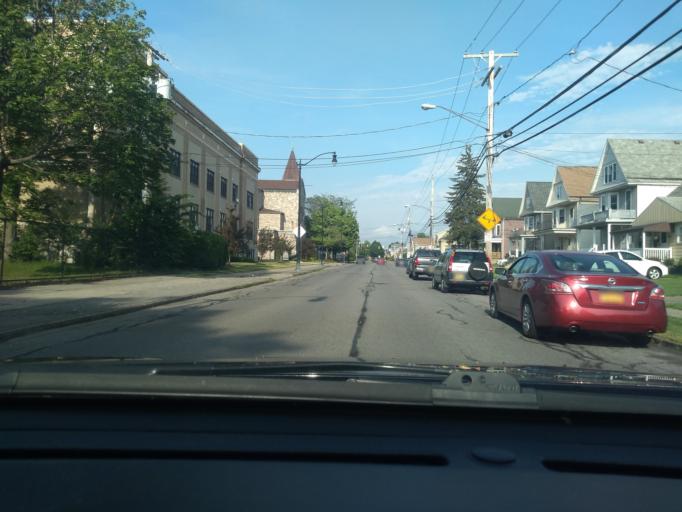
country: US
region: New York
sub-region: Erie County
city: Lackawanna
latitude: 42.8469
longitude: -78.8258
